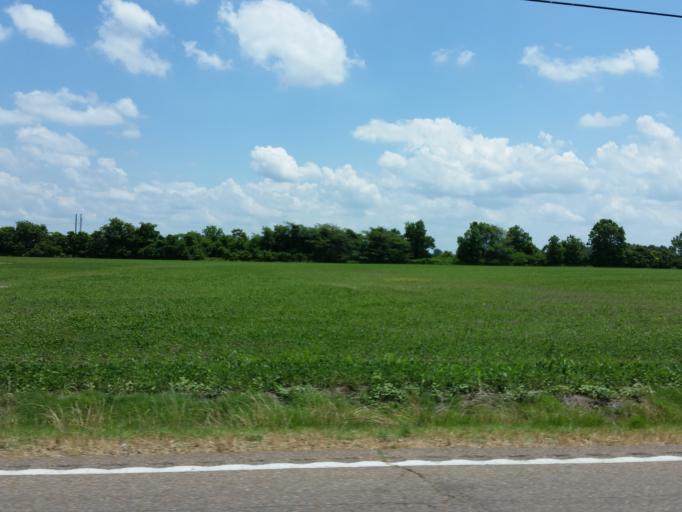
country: US
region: Tennessee
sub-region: Lake County
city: Tiptonville
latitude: 36.3684
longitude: -89.4685
